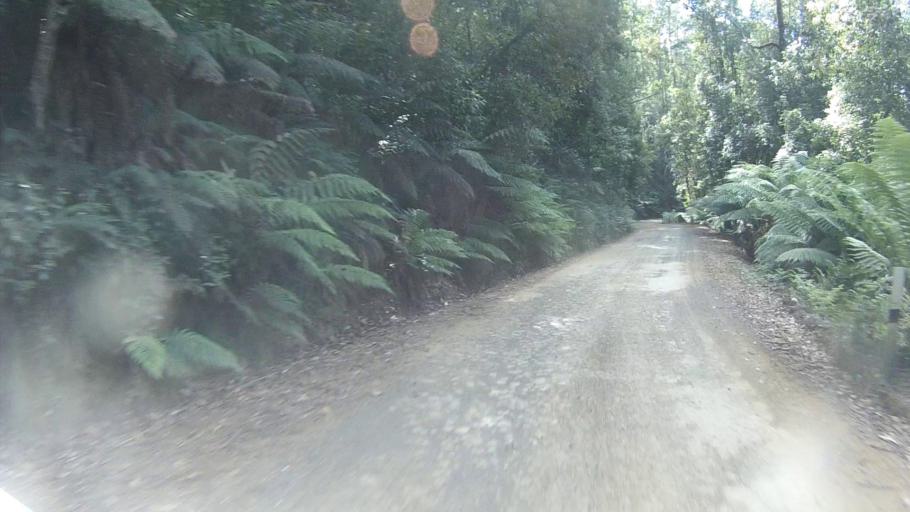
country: AU
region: Tasmania
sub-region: Derwent Valley
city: New Norfolk
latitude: -42.6764
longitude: 146.6930
